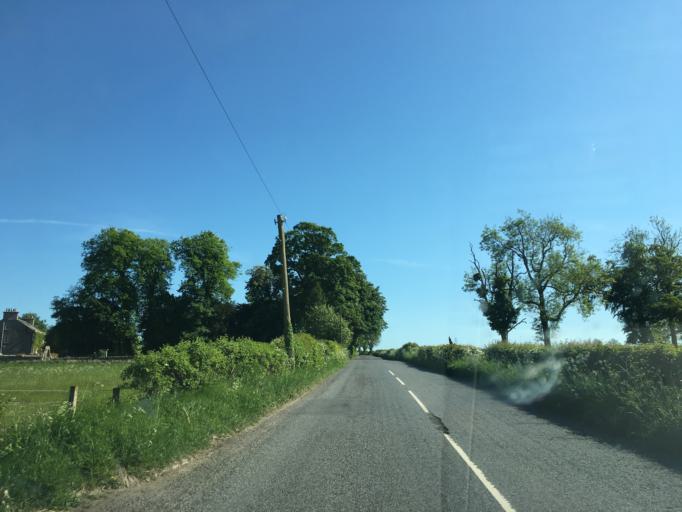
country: GB
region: Scotland
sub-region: Perth and Kinross
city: Methven
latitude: 56.3941
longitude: -3.5387
